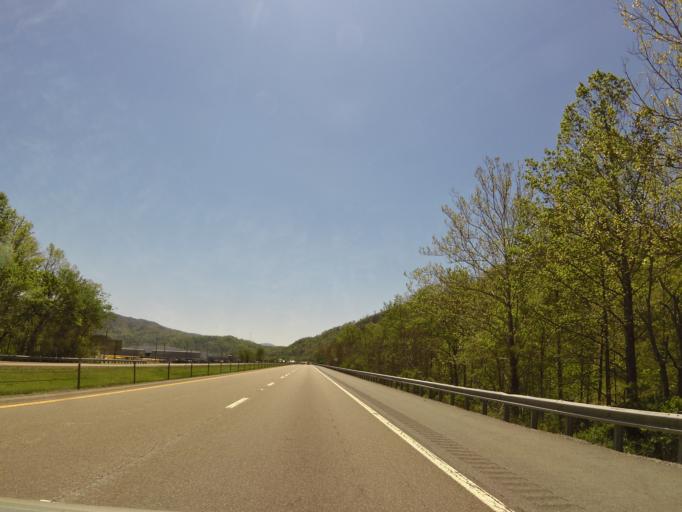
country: US
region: Tennessee
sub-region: Unicoi County
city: Banner Hill
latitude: 36.1336
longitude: -82.4349
